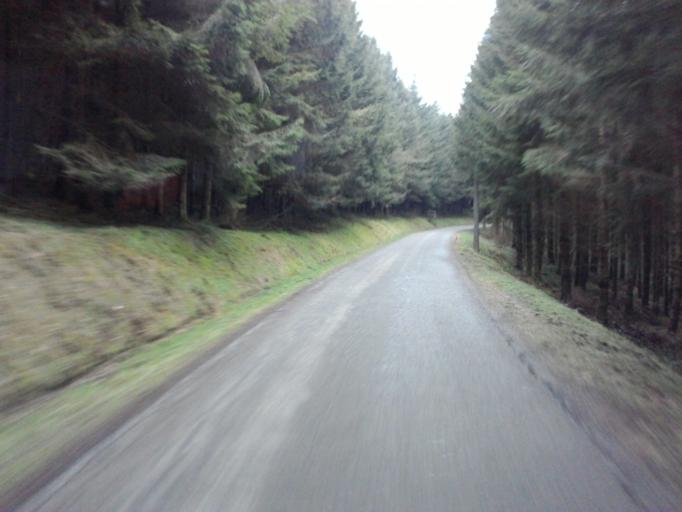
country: BE
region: Wallonia
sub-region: Province de Namur
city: Gedinne
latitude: 50.0282
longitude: 4.8774
